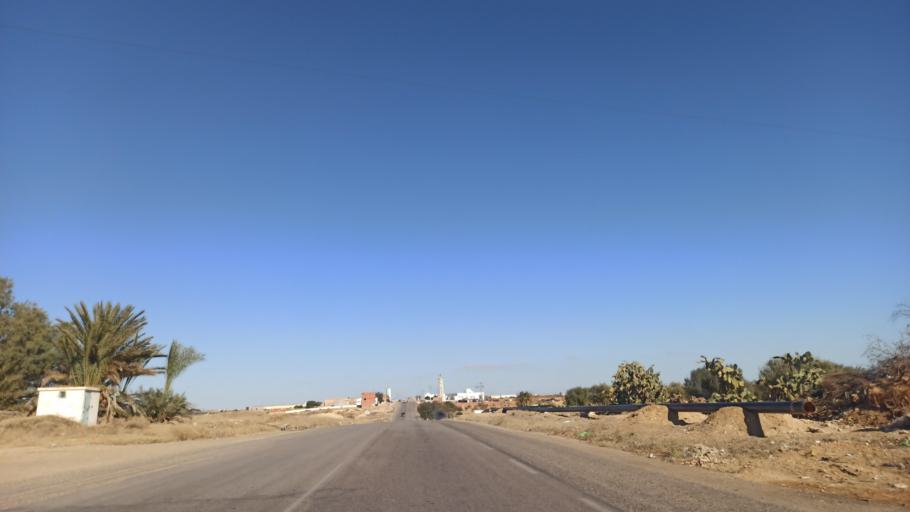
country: TN
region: Sidi Bu Zayd
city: Jilma
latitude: 35.2561
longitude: 9.4002
